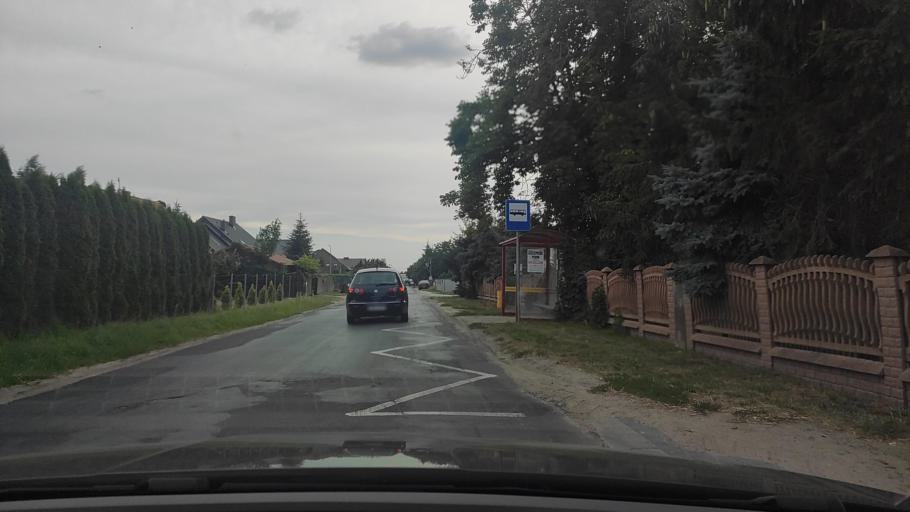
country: PL
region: Greater Poland Voivodeship
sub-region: Powiat poznanski
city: Kleszczewo
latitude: 52.3642
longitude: 17.1369
